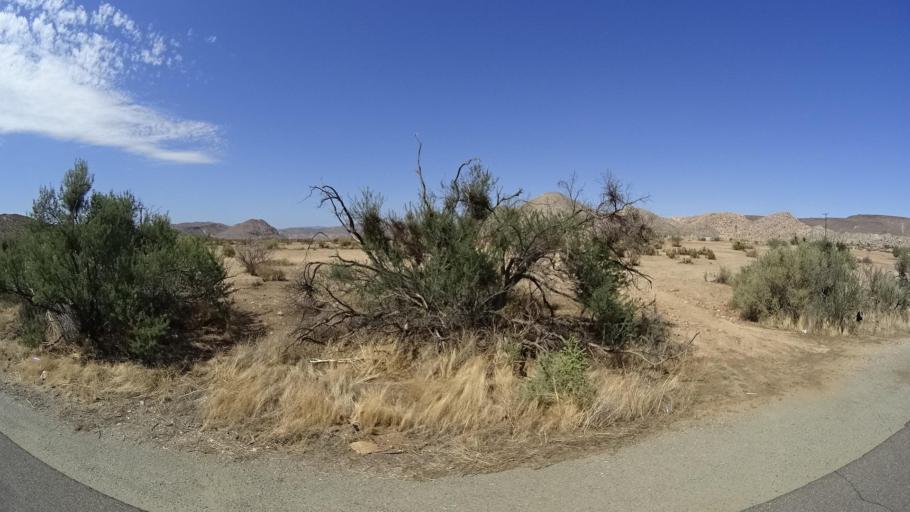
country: MX
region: Baja California
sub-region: Tecate
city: Cereso del Hongo
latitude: 32.6220
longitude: -116.1559
